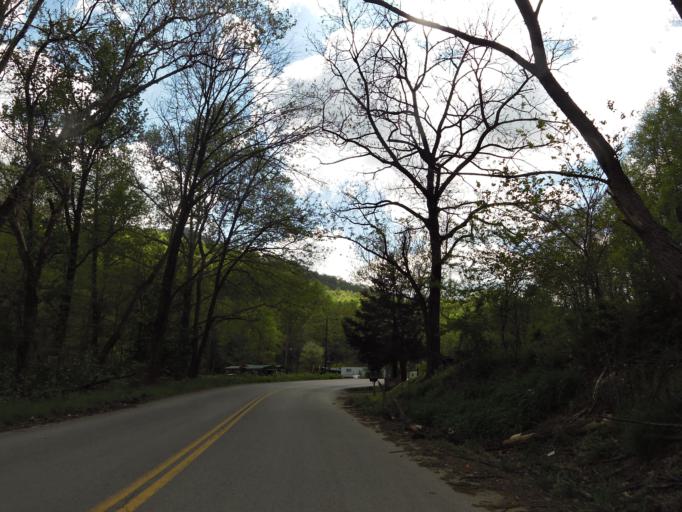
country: US
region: Kentucky
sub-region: Bell County
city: Middlesboro
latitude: 36.6141
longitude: -83.7833
